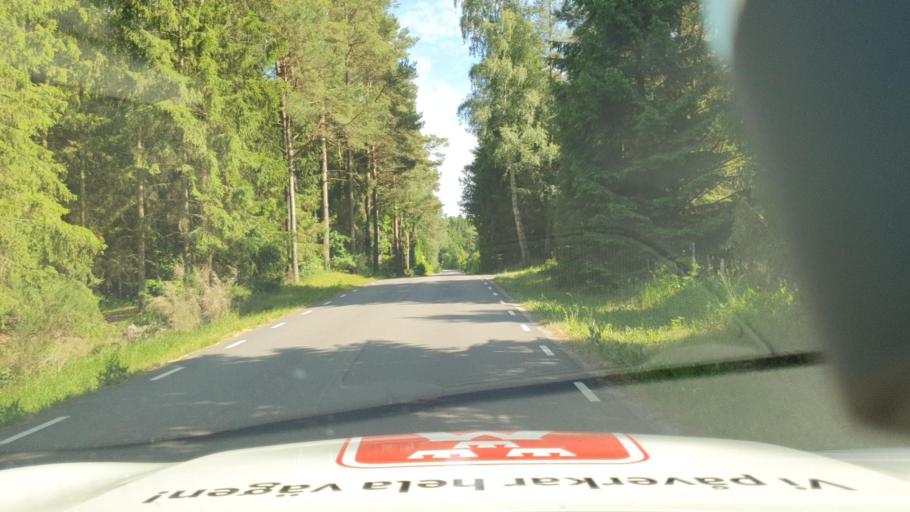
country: SE
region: Skane
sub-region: Sjobo Kommun
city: Blentarp
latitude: 55.5677
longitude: 13.5715
